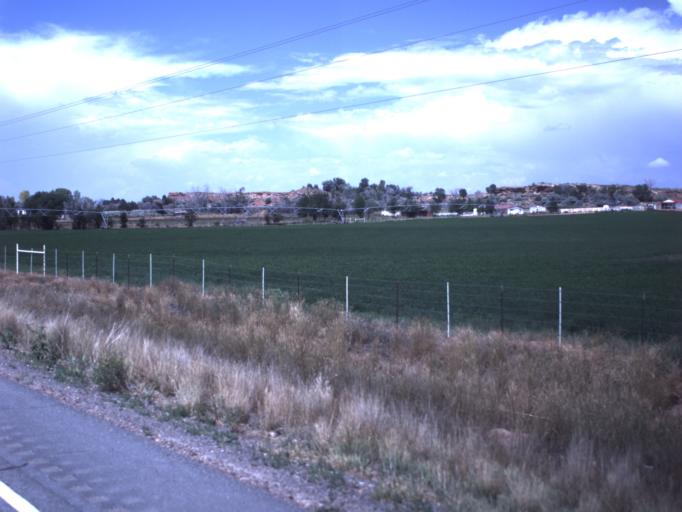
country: US
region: Utah
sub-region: Duchesne County
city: Roosevelt
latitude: 40.3020
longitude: -109.8081
